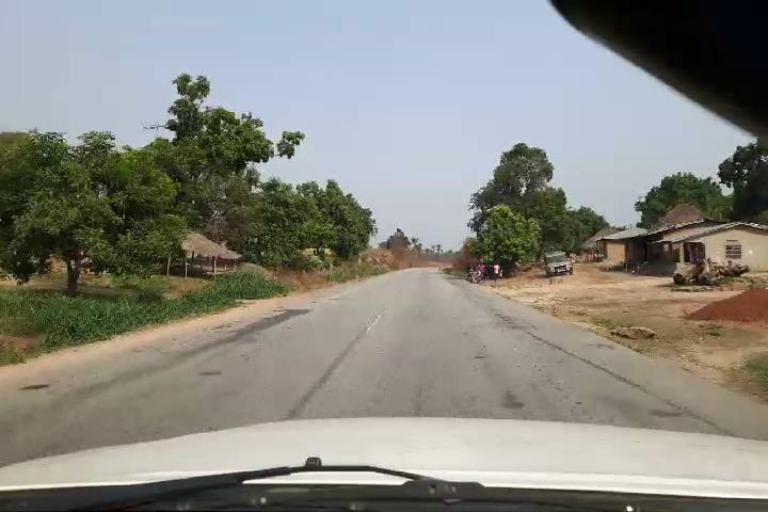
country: SL
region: Southern Province
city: Baiima
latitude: 8.1414
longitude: -11.8996
